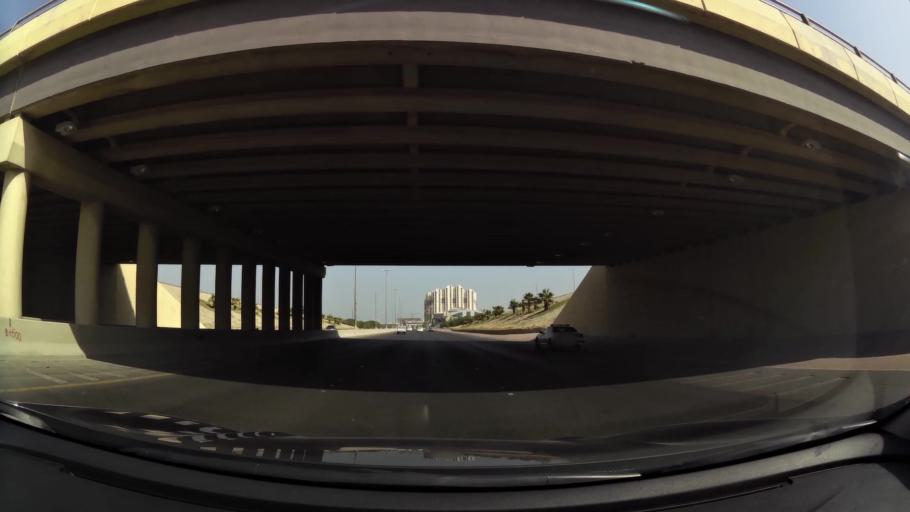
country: KW
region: Mubarak al Kabir
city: Sabah as Salim
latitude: 29.2649
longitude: 48.0670
